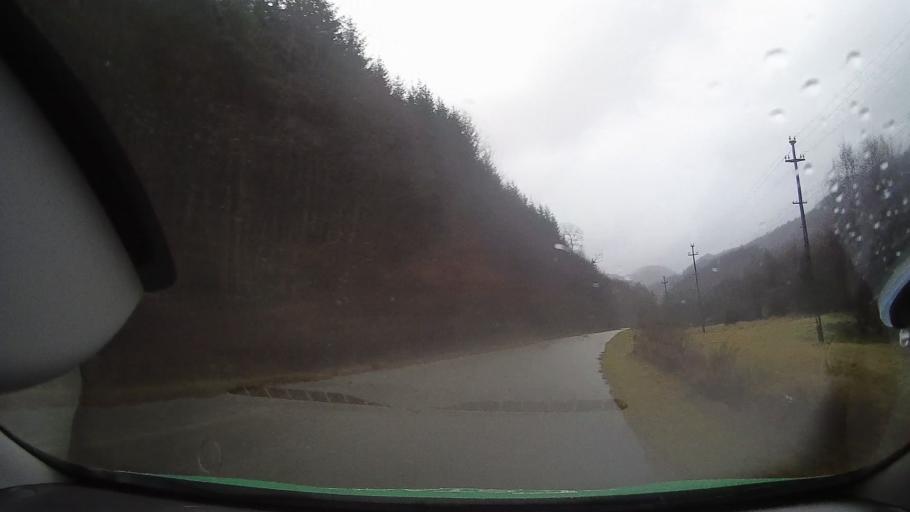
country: RO
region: Alba
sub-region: Comuna Avram Iancu
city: Avram Iancu
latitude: 46.2961
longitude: 22.7560
